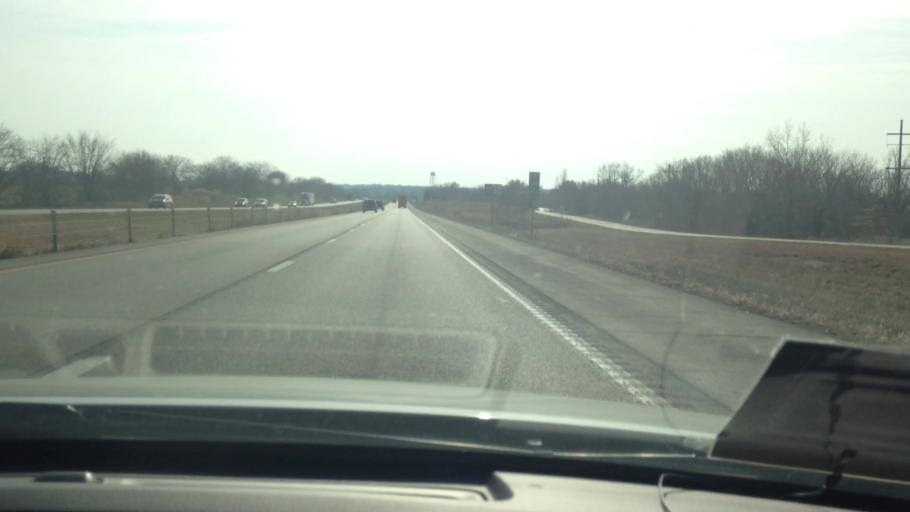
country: US
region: Missouri
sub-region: Cass County
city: Belton
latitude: 38.7798
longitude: -94.4962
